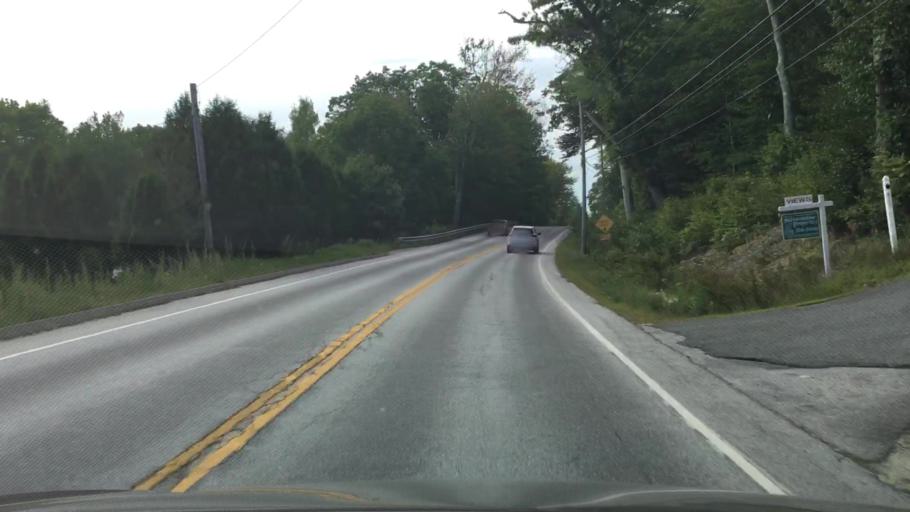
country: US
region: Maine
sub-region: Hancock County
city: Penobscot
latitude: 44.4260
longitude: -68.6003
